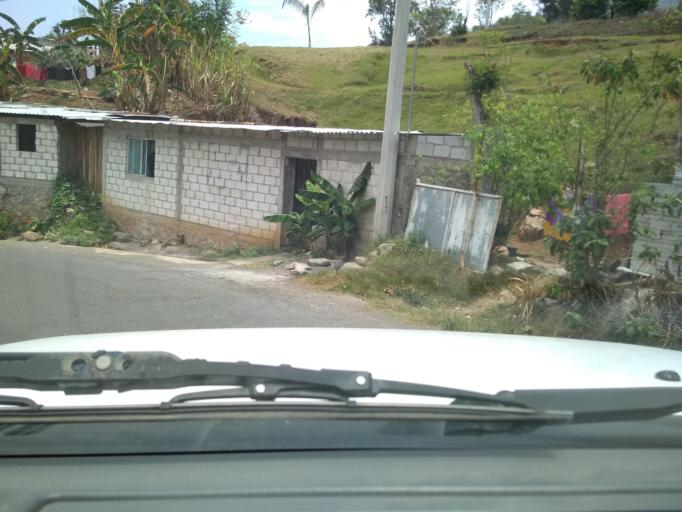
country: MX
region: Veracruz
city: Ciudad Mendoza
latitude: 18.7947
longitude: -97.1794
